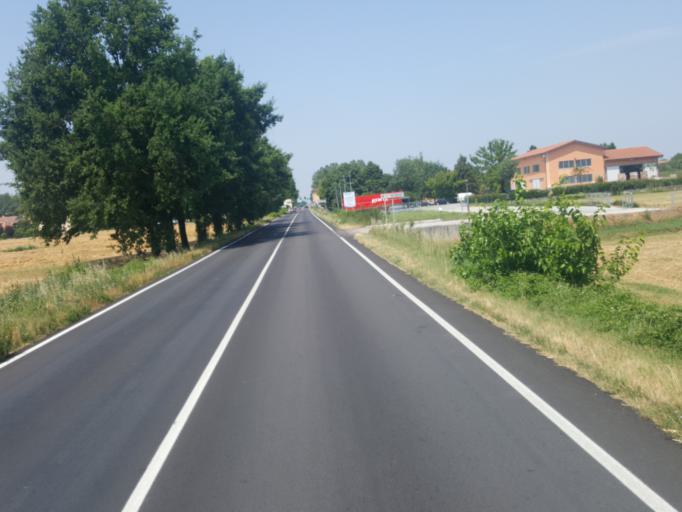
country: IT
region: Emilia-Romagna
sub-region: Provincia di Bologna
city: Calcara
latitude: 44.5616
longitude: 11.1485
